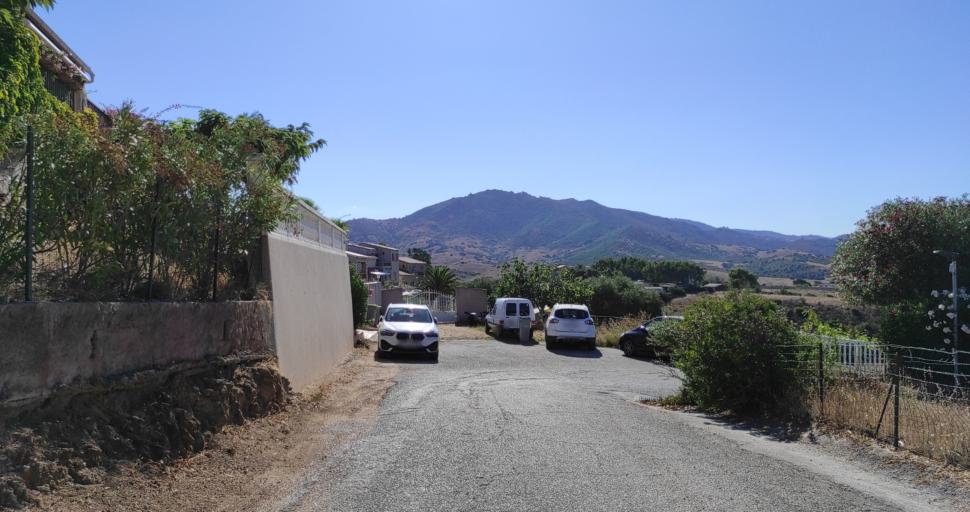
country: FR
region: Corsica
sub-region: Departement de la Corse-du-Sud
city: Alata
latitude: 41.9959
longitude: 8.6701
